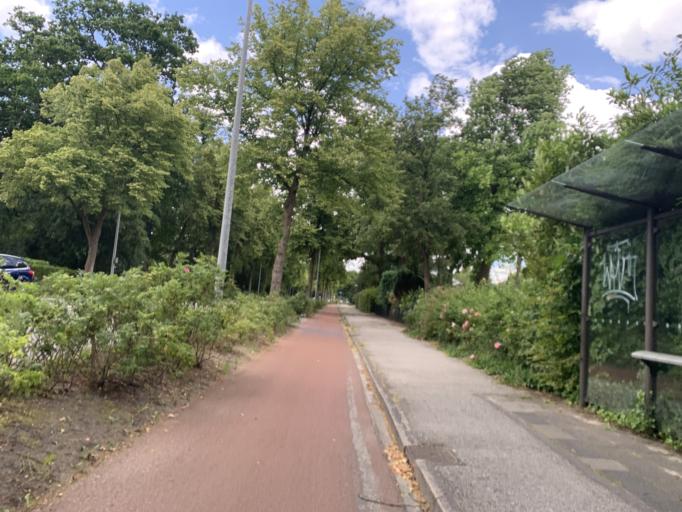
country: NL
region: Groningen
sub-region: Gemeente Haren
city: Haren
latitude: 53.1881
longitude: 6.5860
